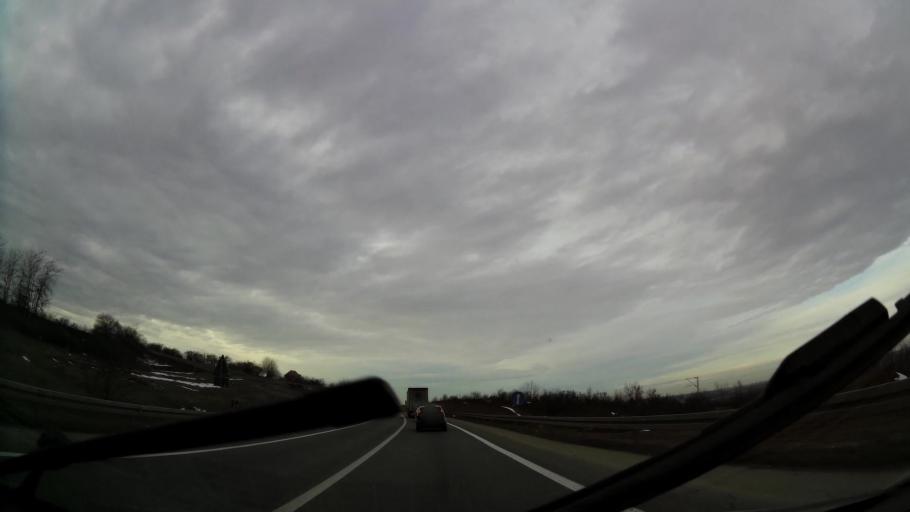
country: RS
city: Ostruznica
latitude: 44.7240
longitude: 20.3573
